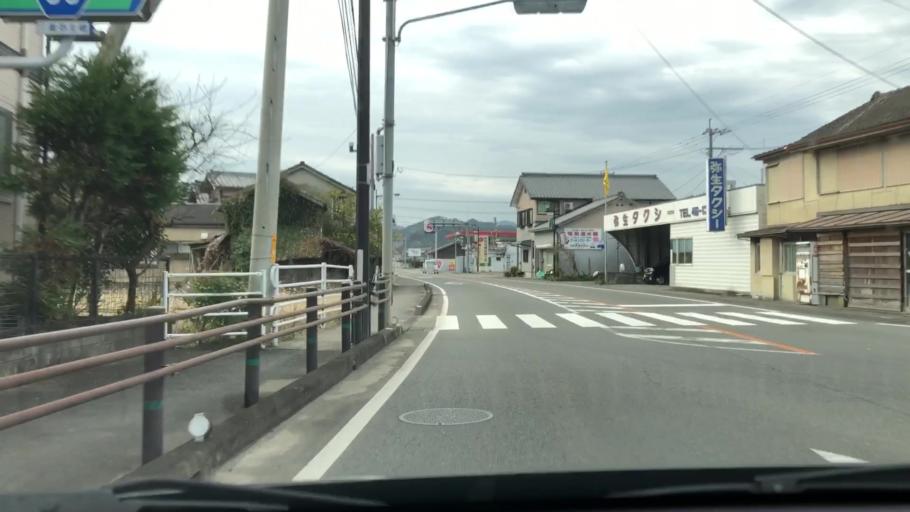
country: JP
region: Oita
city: Saiki
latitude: 32.9686
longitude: 131.8384
